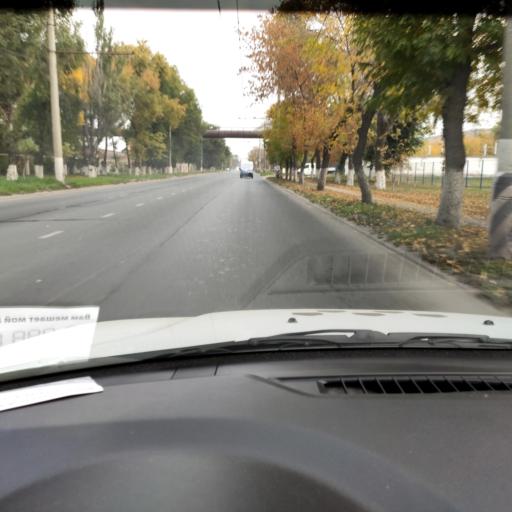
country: RU
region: Samara
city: Tol'yatti
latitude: 53.5578
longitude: 49.4525
